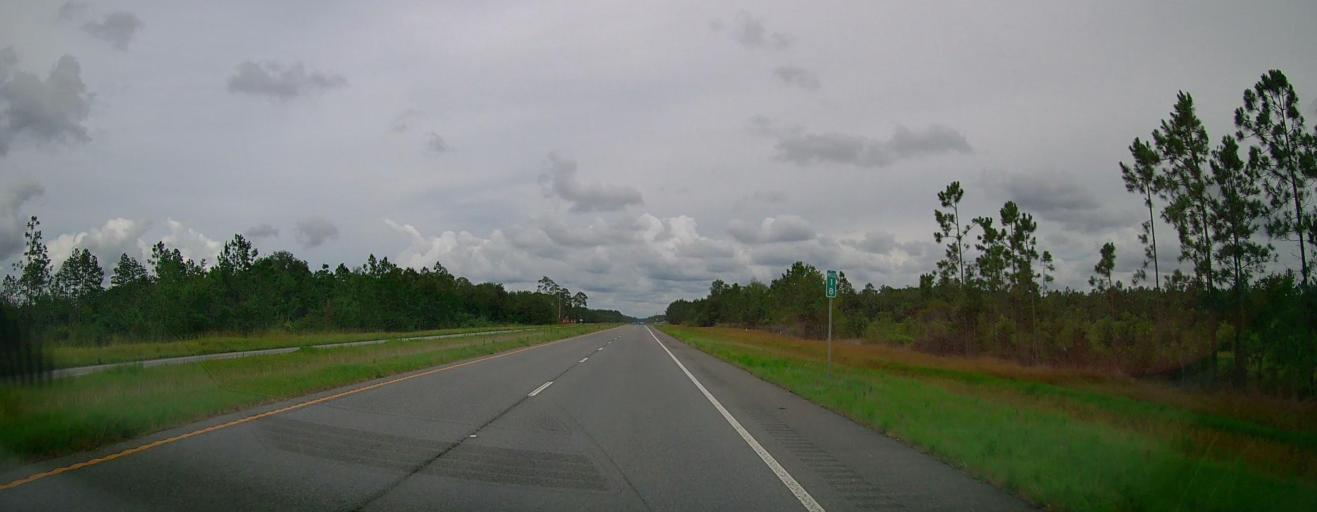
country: US
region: Georgia
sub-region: Appling County
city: Baxley
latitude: 31.7399
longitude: -82.2379
